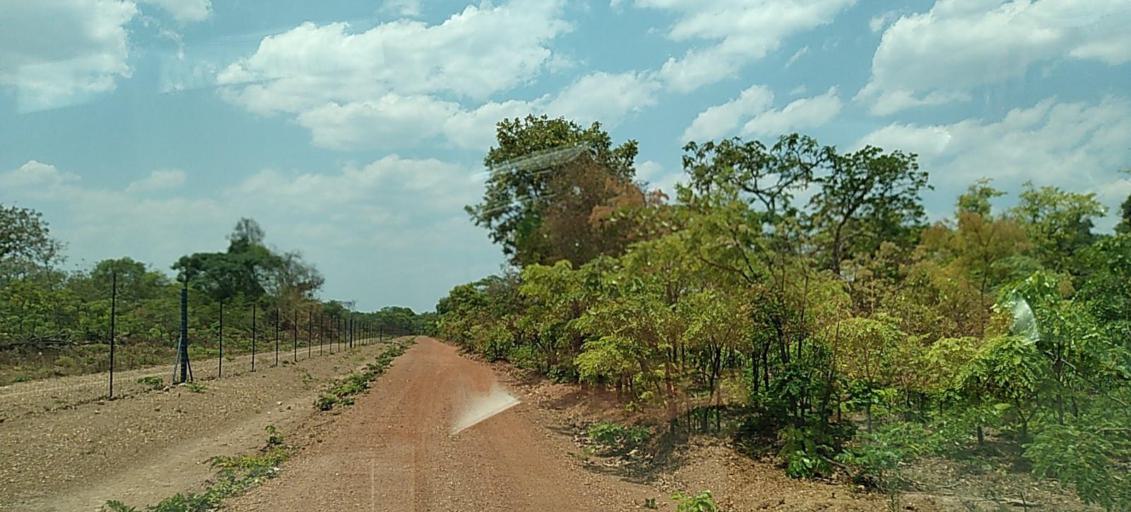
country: ZM
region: Copperbelt
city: Chililabombwe
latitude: -12.5185
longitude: 27.6263
